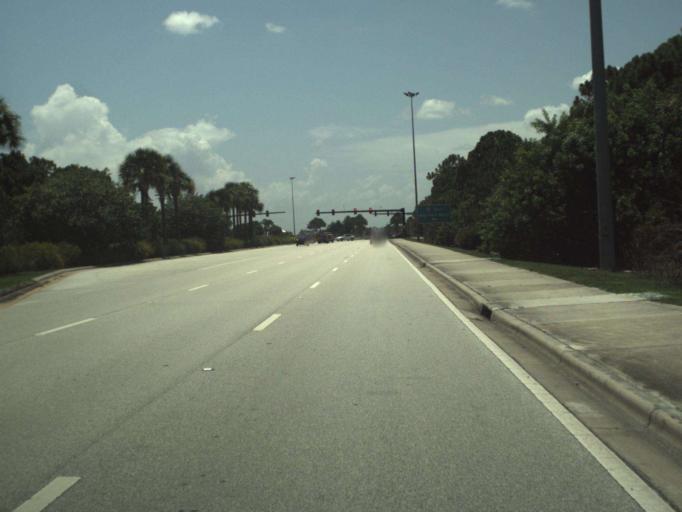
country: US
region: Florida
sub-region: Saint Lucie County
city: Port Saint Lucie
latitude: 27.2645
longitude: -80.4226
